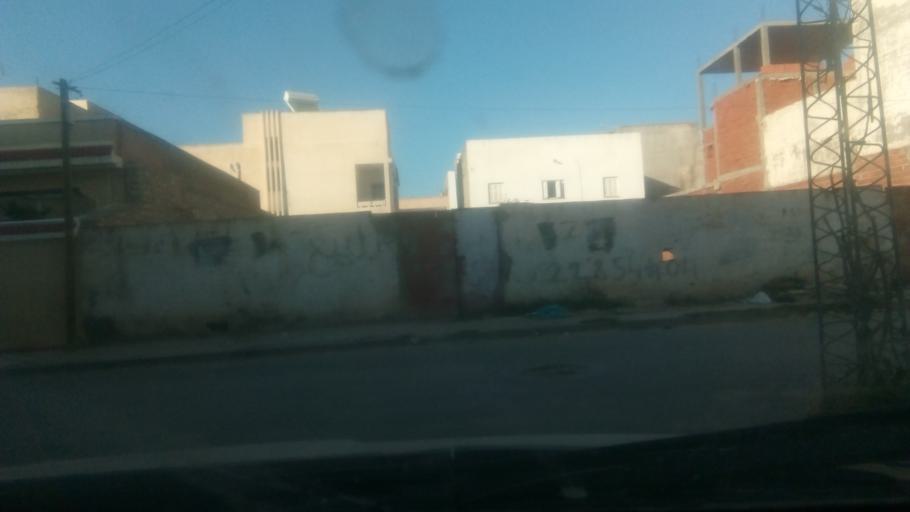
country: TN
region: Al Qayrawan
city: Kairouan
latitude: 35.6678
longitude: 10.0793
